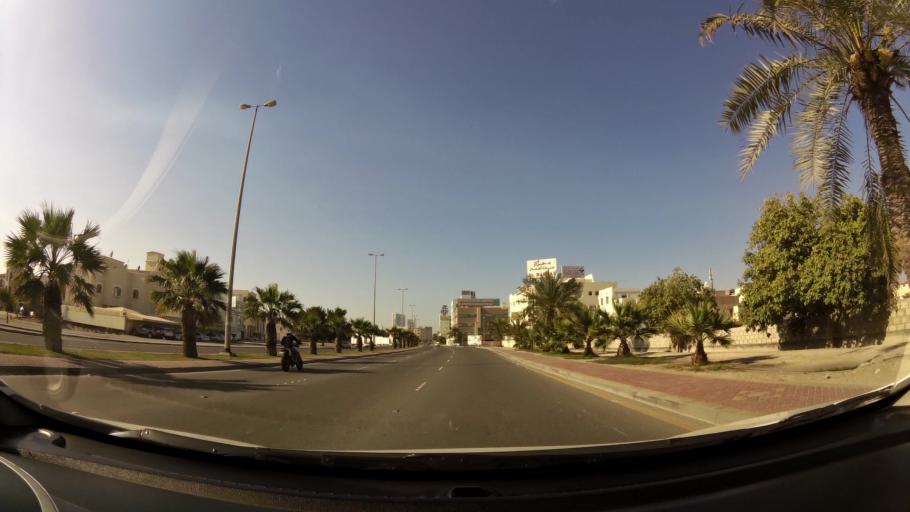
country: BH
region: Manama
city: Manama
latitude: 26.2072
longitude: 50.5673
